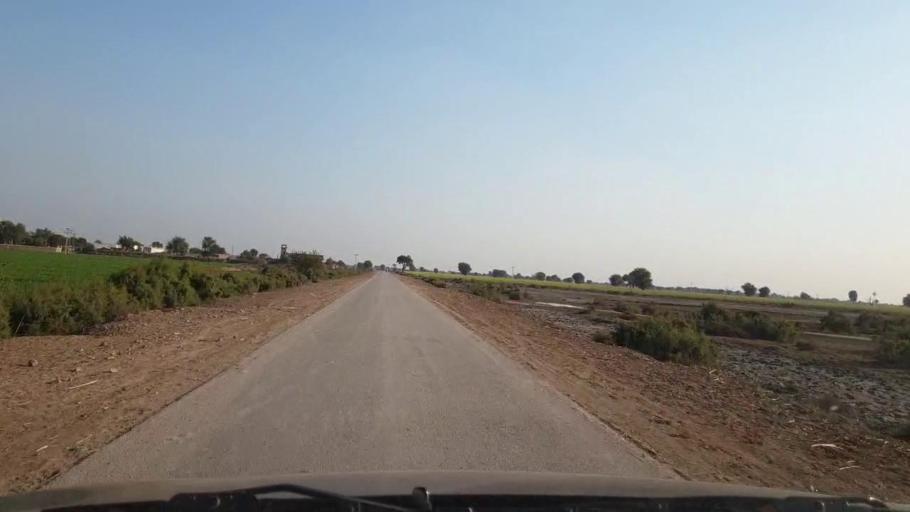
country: PK
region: Sindh
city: Jhol
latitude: 25.9442
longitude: 68.9072
